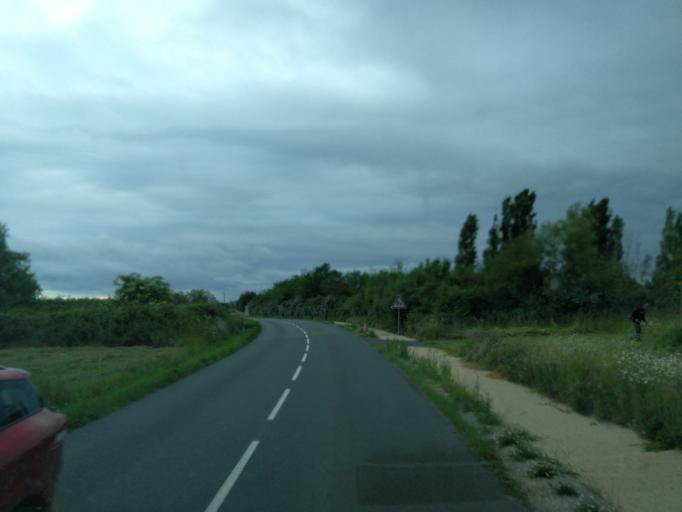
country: FR
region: Pays de la Loire
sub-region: Departement de la Vendee
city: Vix
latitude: 46.3713
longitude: -0.9119
